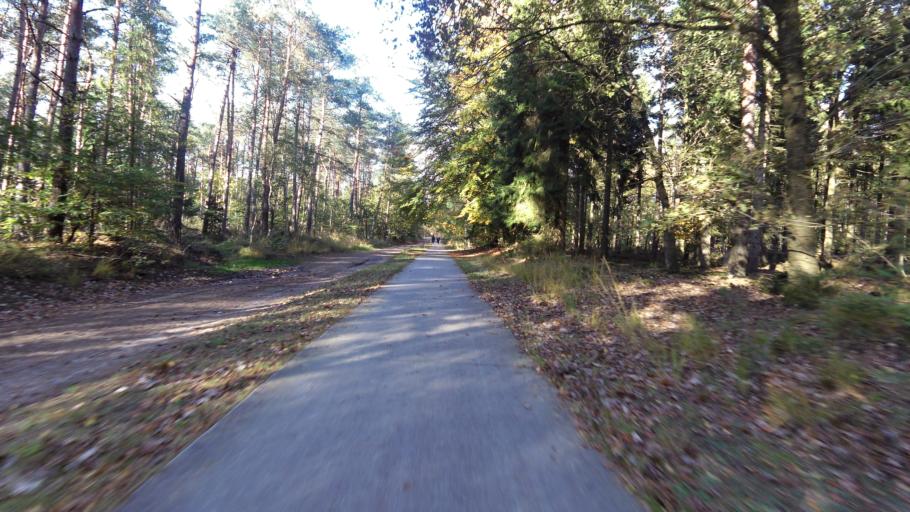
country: NL
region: Gelderland
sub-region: Gemeente Heerde
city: Heerde
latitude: 52.3884
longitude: 5.9985
